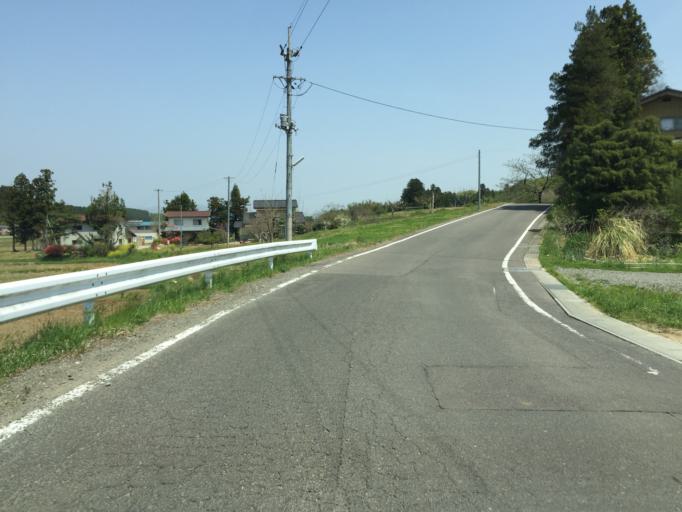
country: JP
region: Fukushima
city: Fukushima-shi
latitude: 37.6941
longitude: 140.4440
